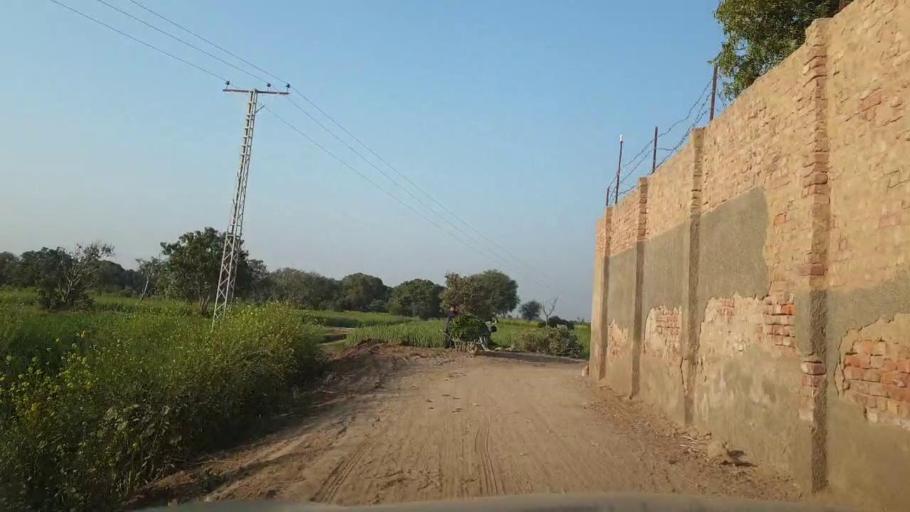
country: PK
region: Sindh
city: Tando Allahyar
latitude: 25.5456
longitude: 68.8433
